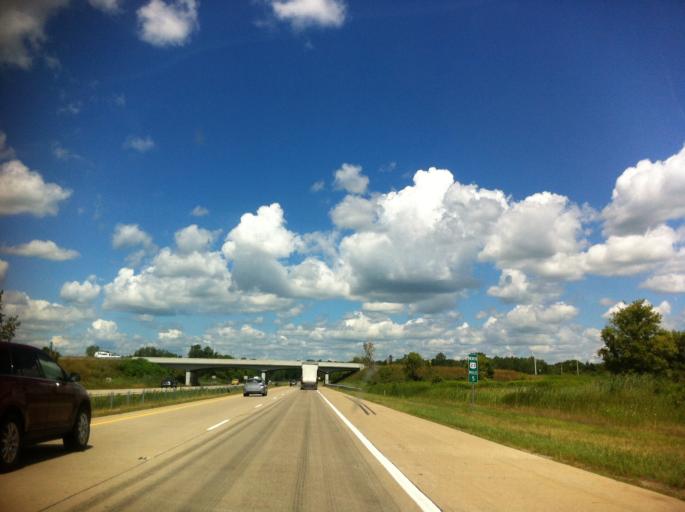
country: US
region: Michigan
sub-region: Monroe County
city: Lambertville
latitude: 41.7943
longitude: -83.6918
